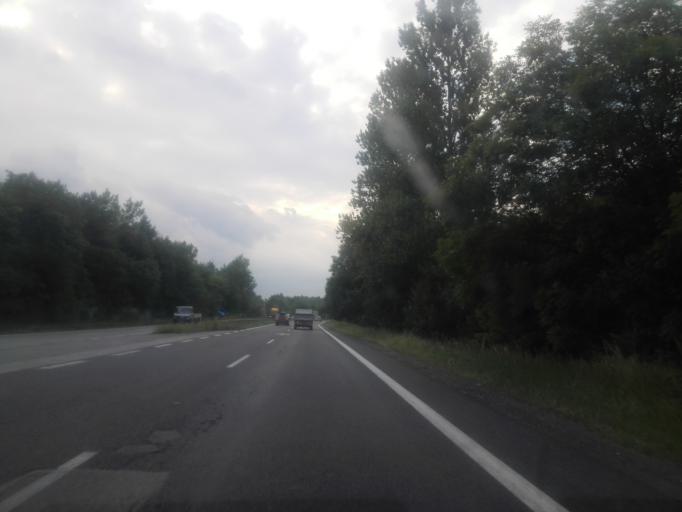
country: PL
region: Silesian Voivodeship
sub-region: Powiat bedzinski
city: Siewierz
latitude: 50.4837
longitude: 19.2198
